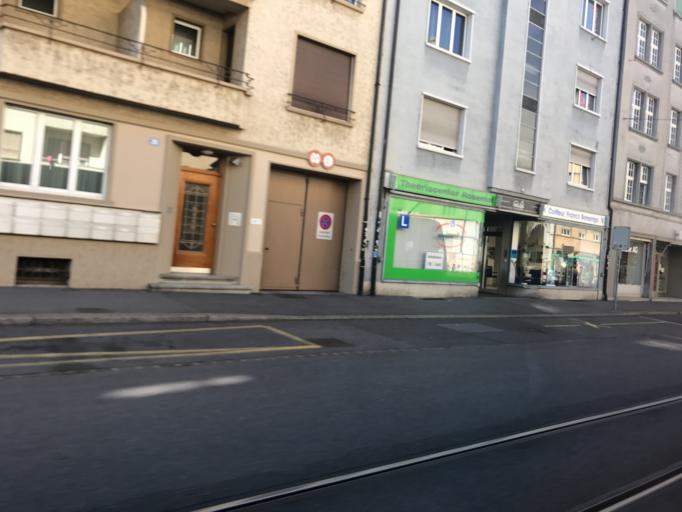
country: CH
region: Basel-Landschaft
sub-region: Bezirk Arlesheim
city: Birsfelden
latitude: 47.5652
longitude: 7.6042
